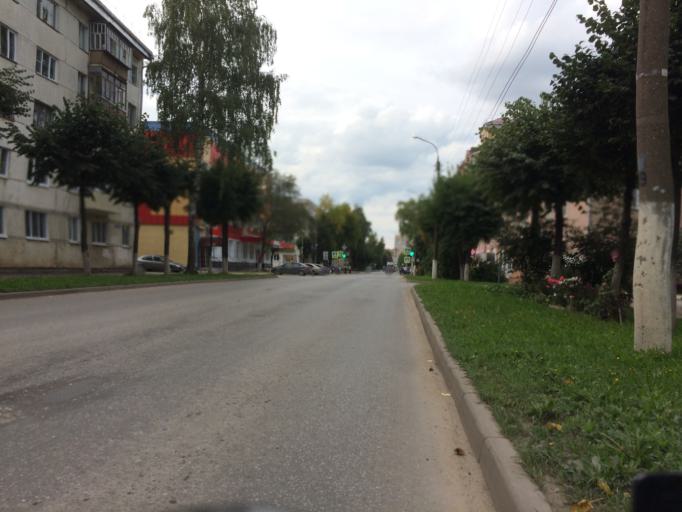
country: RU
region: Mariy-El
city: Yoshkar-Ola
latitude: 56.6350
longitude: 47.8716
